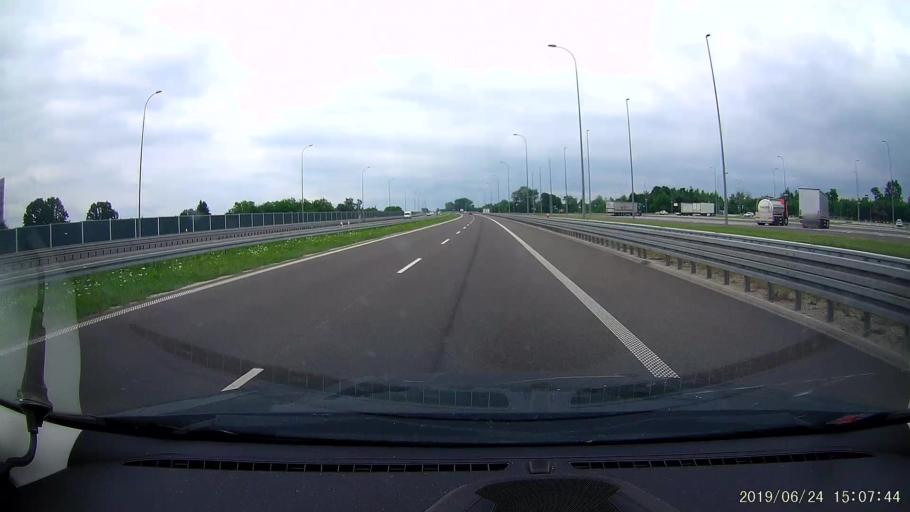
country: PL
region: Subcarpathian Voivodeship
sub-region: Powiat lancucki
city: Czarna
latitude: 50.0894
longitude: 22.1746
